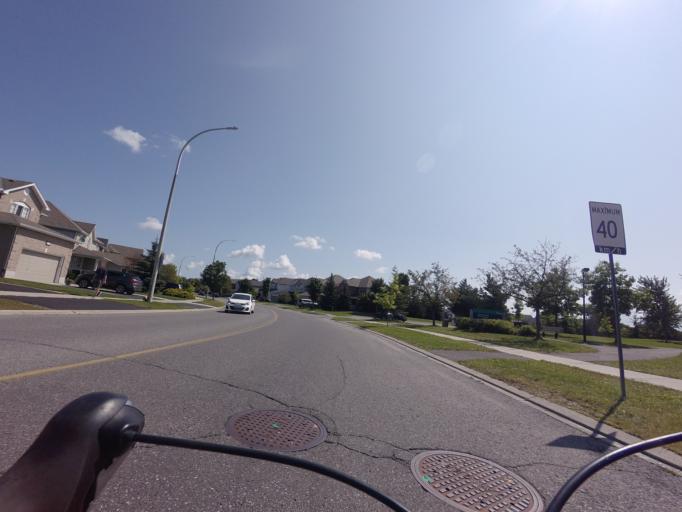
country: CA
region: Ontario
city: Bells Corners
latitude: 45.2840
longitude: -75.8503
